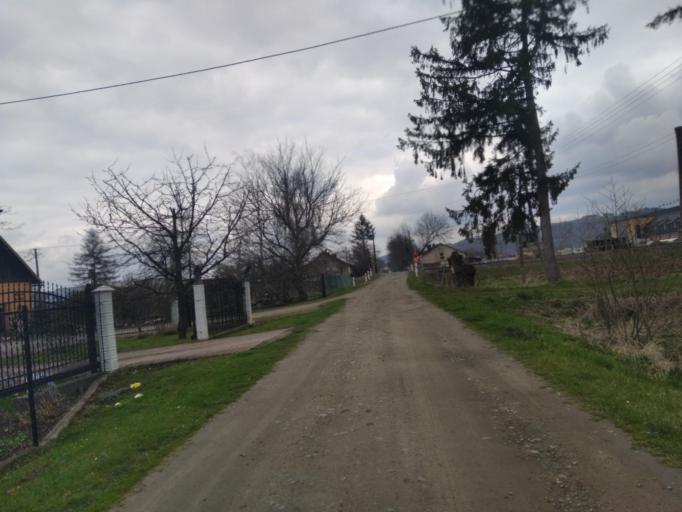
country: PL
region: Subcarpathian Voivodeship
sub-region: Powiat strzyzowski
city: Strzyzow
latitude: 49.8699
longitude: 21.7534
